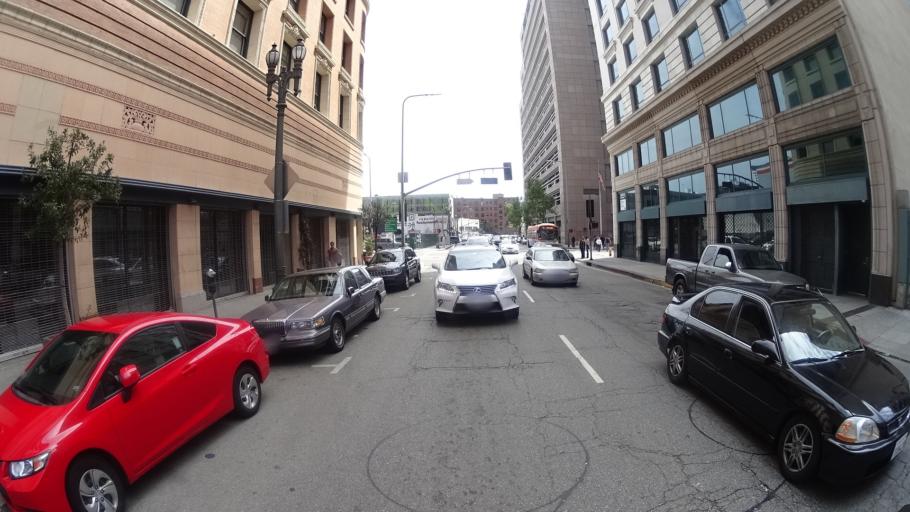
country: US
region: California
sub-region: Los Angeles County
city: Los Angeles
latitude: 34.0505
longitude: -118.2473
